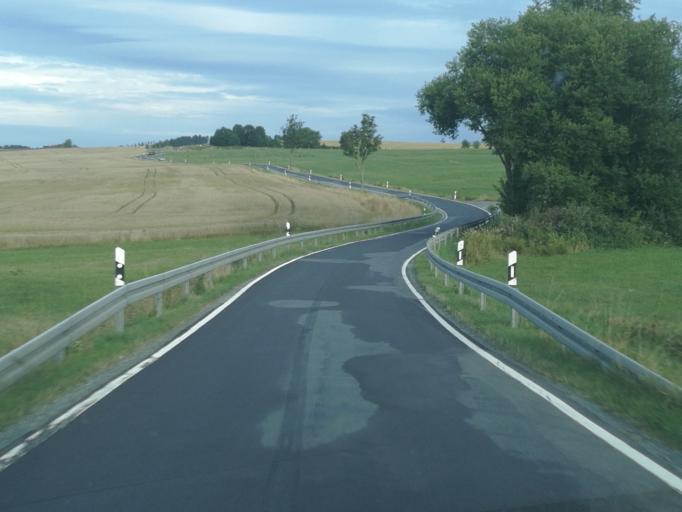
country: DE
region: Saxony
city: Triebel
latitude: 50.3337
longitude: 12.0980
